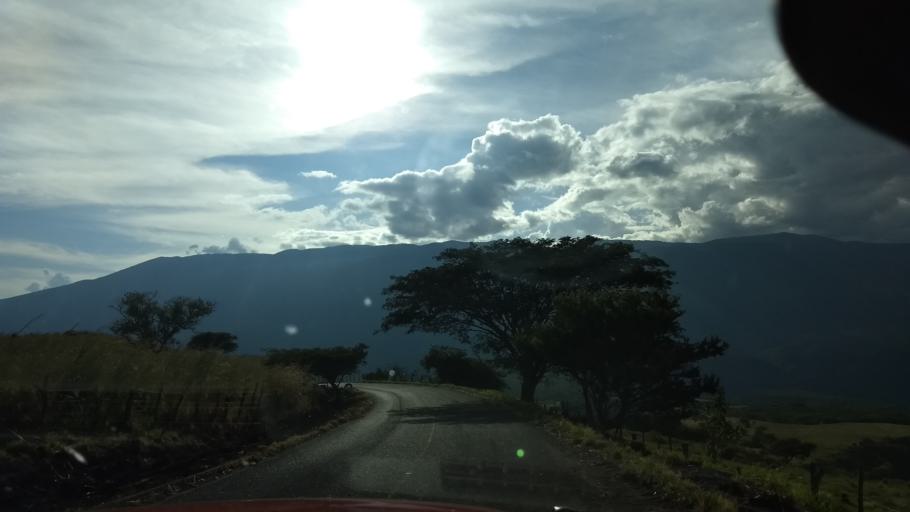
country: MX
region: Colima
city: Suchitlan
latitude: 19.4605
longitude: -103.7910
